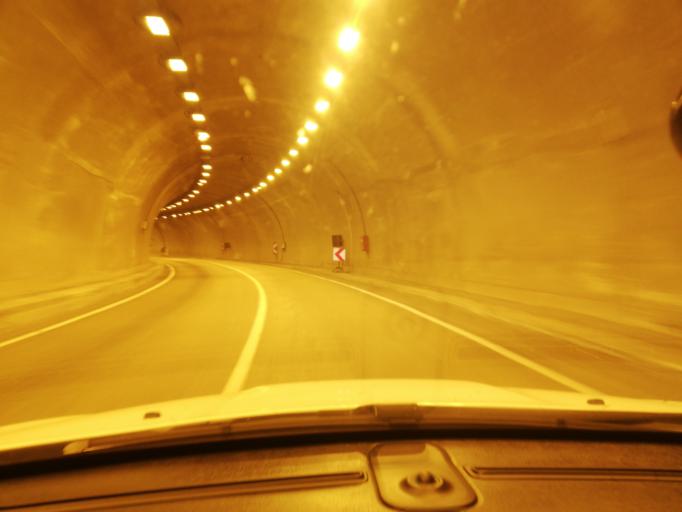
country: TR
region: Karabuk
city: Karabuk
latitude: 41.1533
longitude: 32.5267
